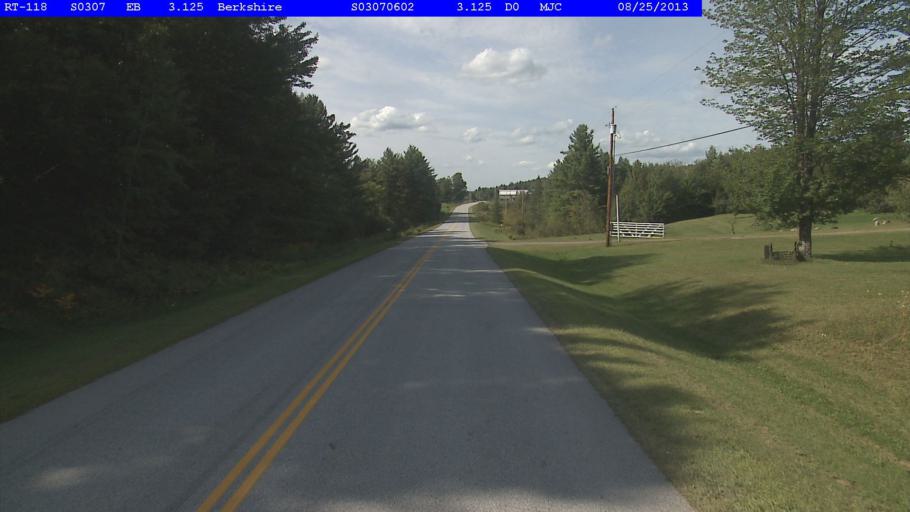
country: US
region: Vermont
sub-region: Franklin County
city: Enosburg Falls
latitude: 44.9606
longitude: -72.7574
